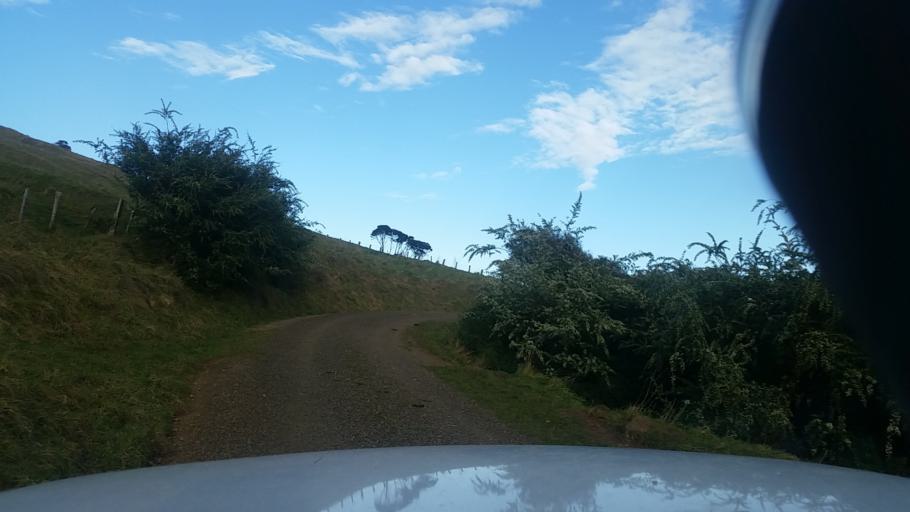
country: NZ
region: Canterbury
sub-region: Christchurch City
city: Christchurch
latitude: -43.7602
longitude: 172.9901
